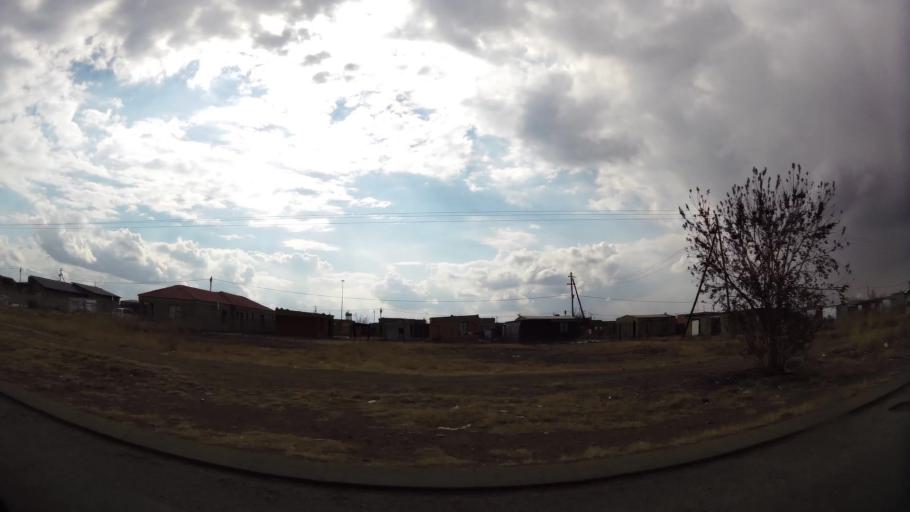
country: ZA
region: Gauteng
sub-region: Sedibeng District Municipality
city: Vanderbijlpark
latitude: -26.6819
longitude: 27.7841
